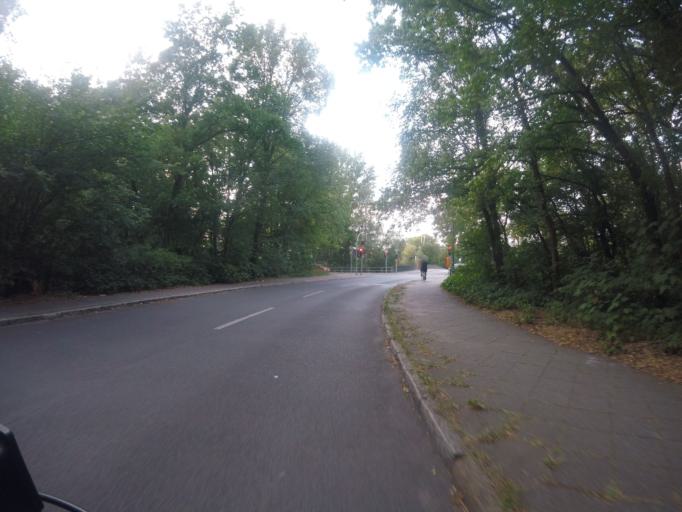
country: DE
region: Berlin
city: Siemensstadt
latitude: 52.5483
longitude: 13.2705
